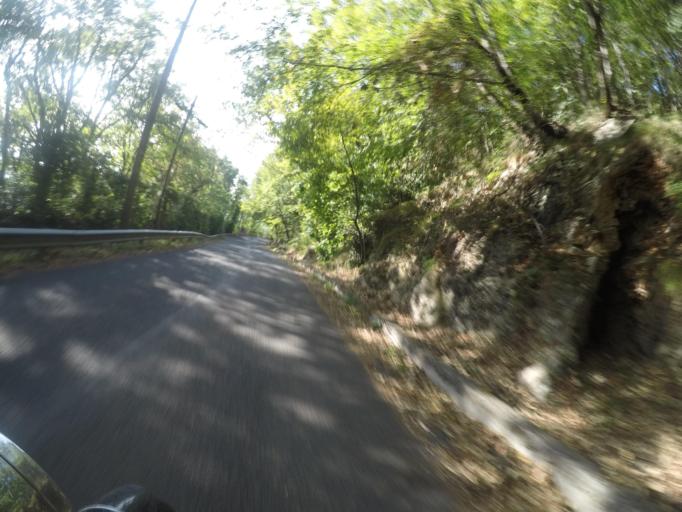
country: IT
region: Tuscany
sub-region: Provincia di Massa-Carrara
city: Massa
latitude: 44.0679
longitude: 10.1187
